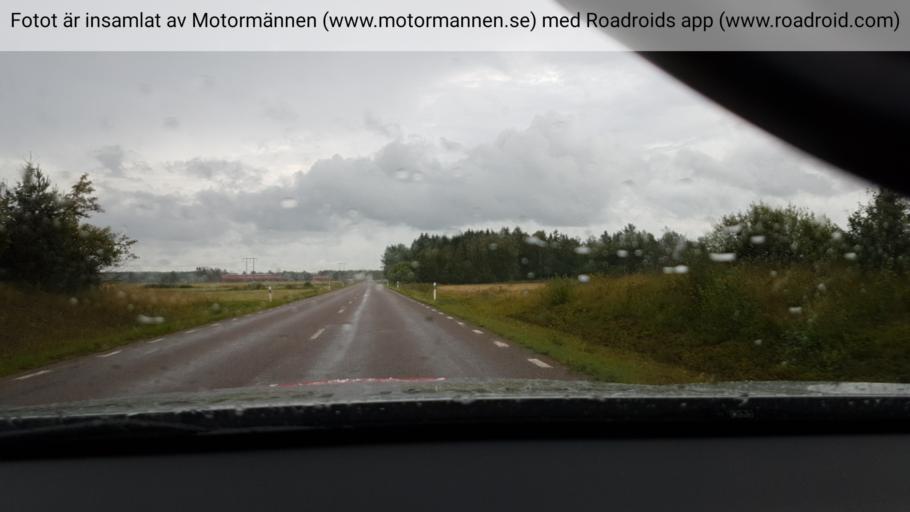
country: SE
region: Uppsala
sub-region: Tierps Kommun
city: Karlholmsbruk
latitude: 60.4889
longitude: 17.7275
